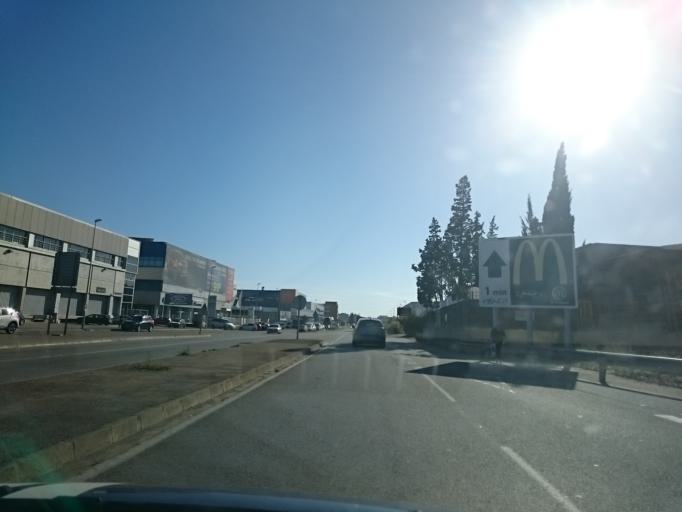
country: ES
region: Catalonia
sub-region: Provincia de Barcelona
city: Sant Boi de Llobregat
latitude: 41.3284
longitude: 2.0369
